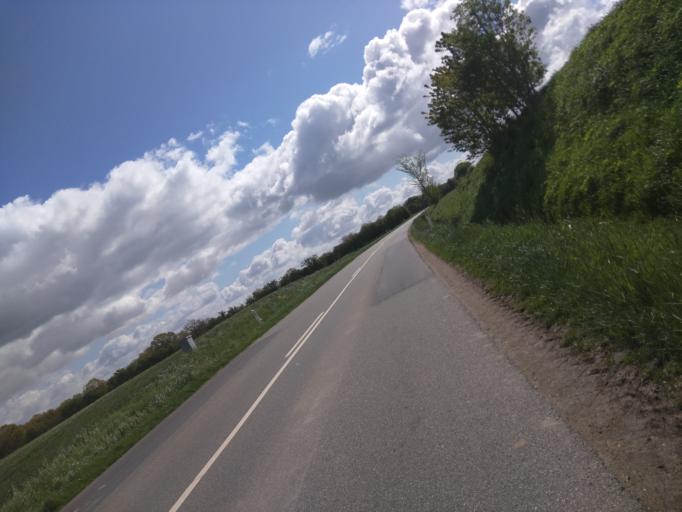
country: DK
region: Central Jutland
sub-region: Silkeborg Kommune
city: Kjellerup
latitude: 56.2770
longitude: 9.5046
